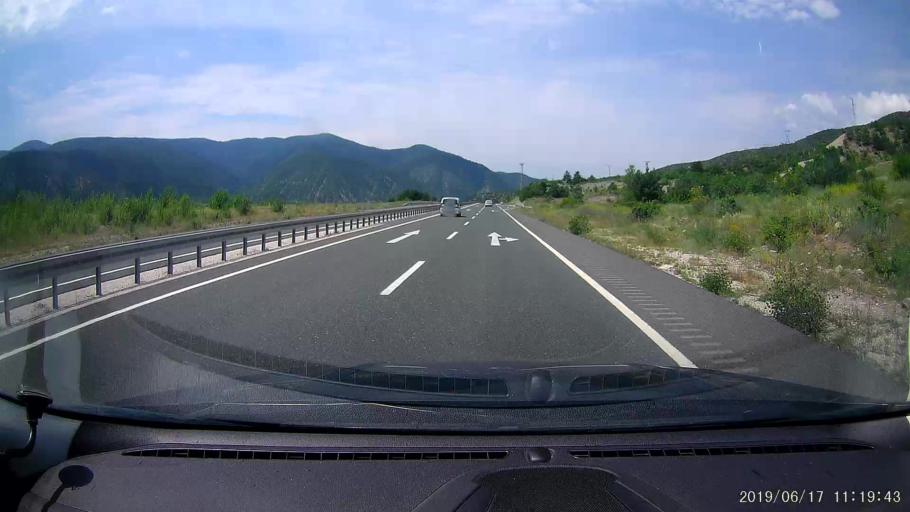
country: TR
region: Cankiri
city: Yaprakli
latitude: 40.9229
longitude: 33.8213
